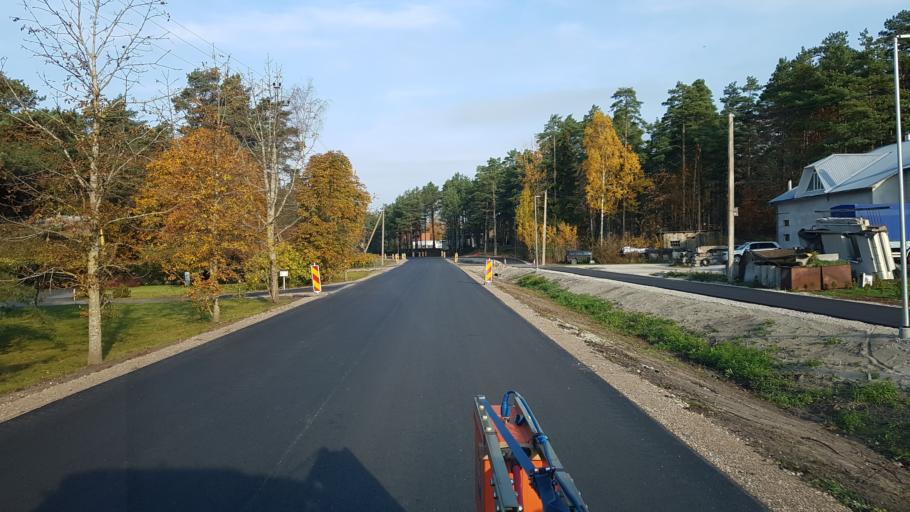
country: EE
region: Paernumaa
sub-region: Paikuse vald
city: Paikuse
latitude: 58.3526
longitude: 24.6194
